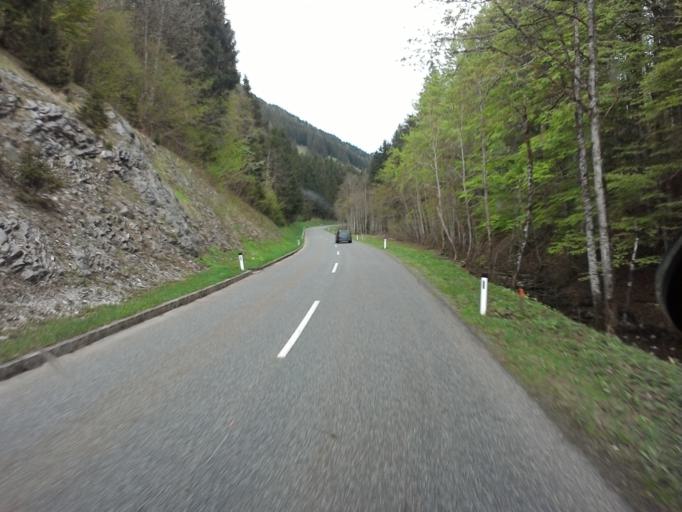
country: AT
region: Styria
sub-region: Politischer Bezirk Liezen
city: Hall
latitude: 47.7068
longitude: 14.4465
